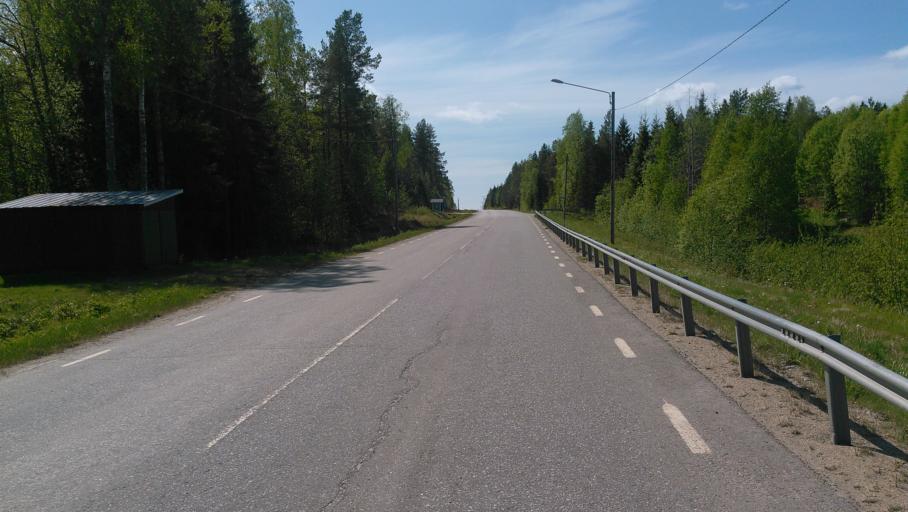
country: SE
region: Vaesterbotten
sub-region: Umea Kommun
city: Roback
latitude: 63.8626
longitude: 20.0112
